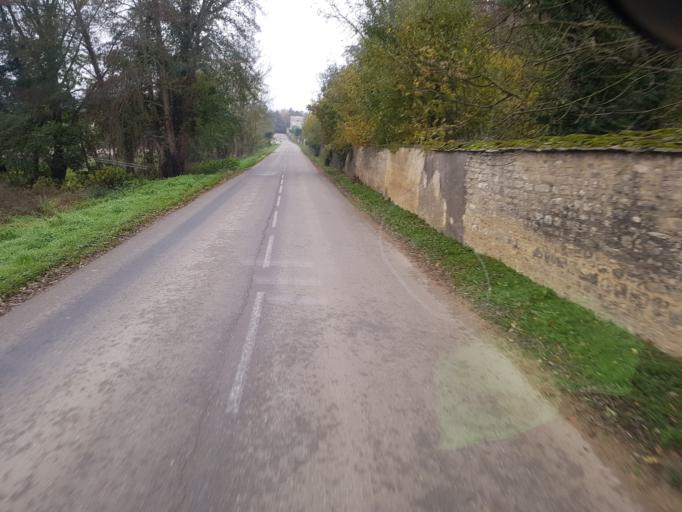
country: FR
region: Bourgogne
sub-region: Departement de la Cote-d'Or
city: Arc-sur-Tille
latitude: 47.3679
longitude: 5.1972
